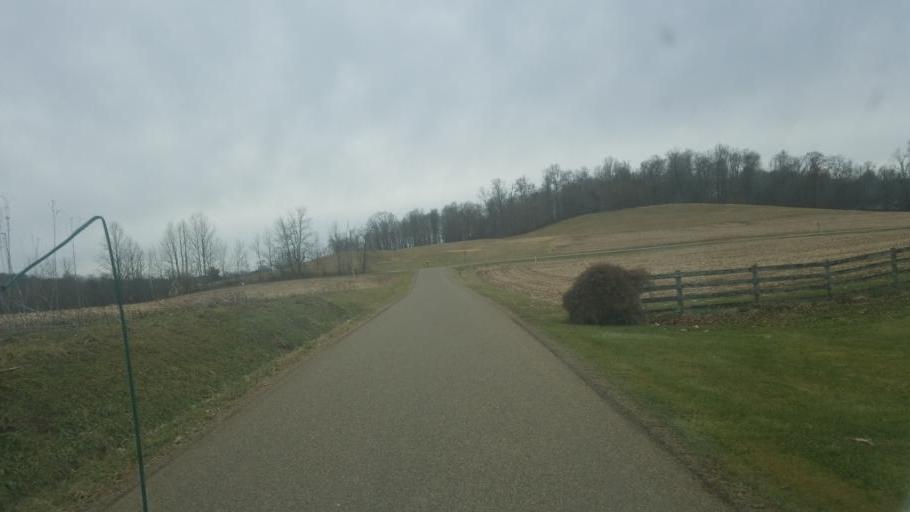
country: US
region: Ohio
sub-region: Richland County
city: Lincoln Heights
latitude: 40.6942
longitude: -82.3937
